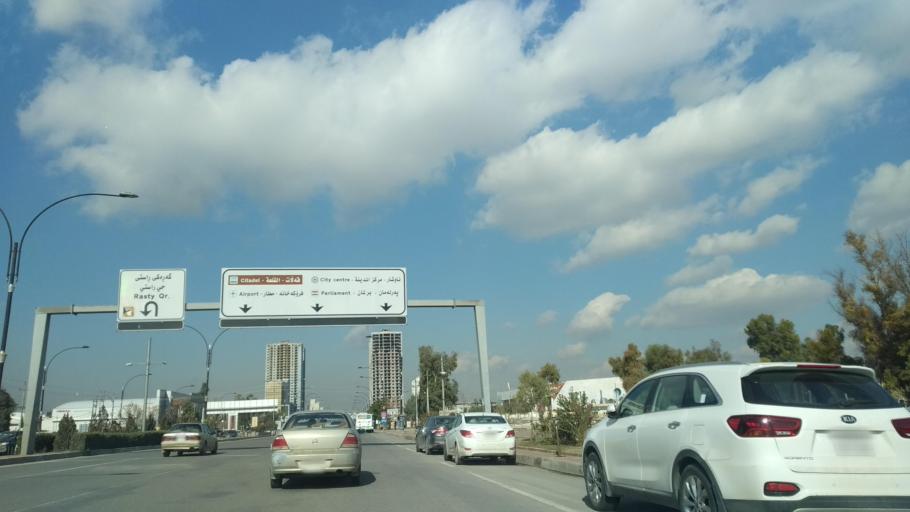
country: IQ
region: Arbil
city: Erbil
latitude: 36.1408
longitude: 44.0208
